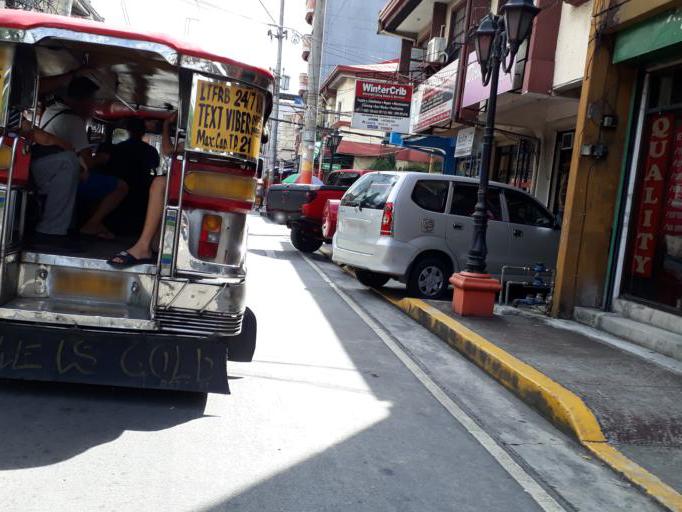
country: PH
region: Metro Manila
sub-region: City of Manila
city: Manila
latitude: 14.6184
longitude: 120.9958
